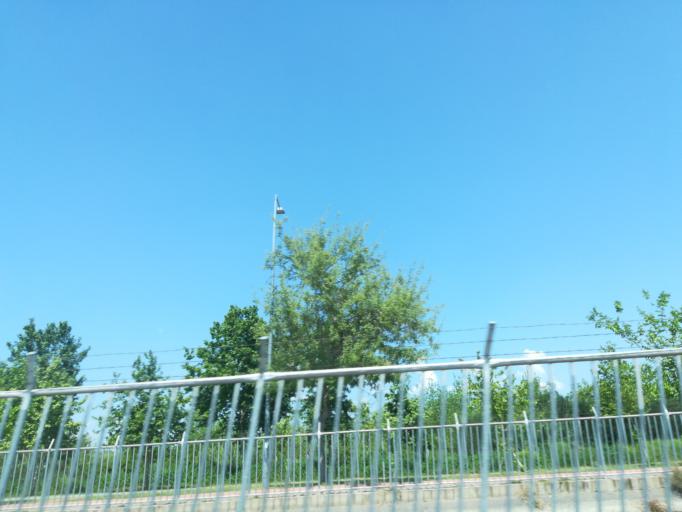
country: TR
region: Adana
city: Adana
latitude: 37.0228
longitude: 35.3699
